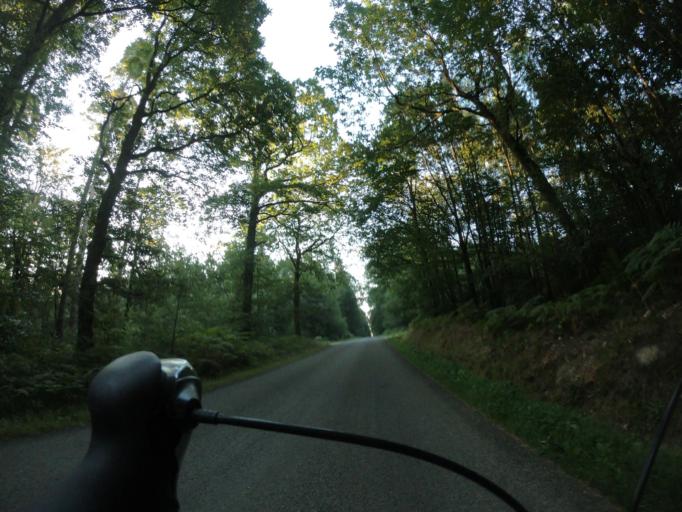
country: FR
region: Lower Normandy
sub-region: Departement de l'Orne
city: Tesse-la-Madeleine
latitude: 48.5581
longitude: -0.3893
